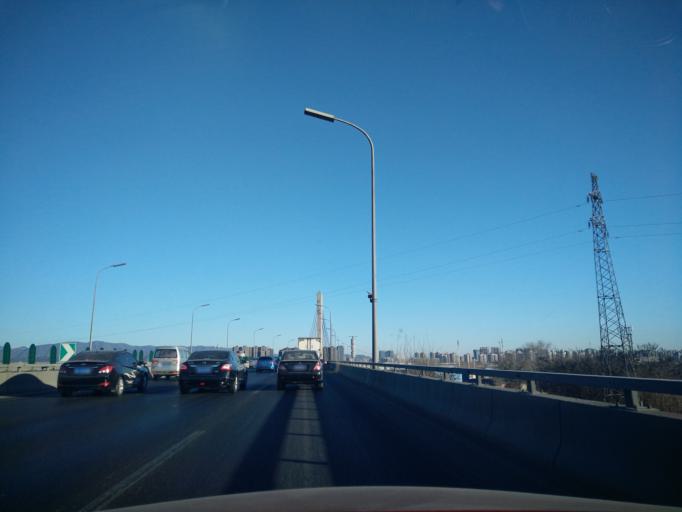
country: CN
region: Beijing
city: Lugu
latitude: 39.8766
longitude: 116.2020
